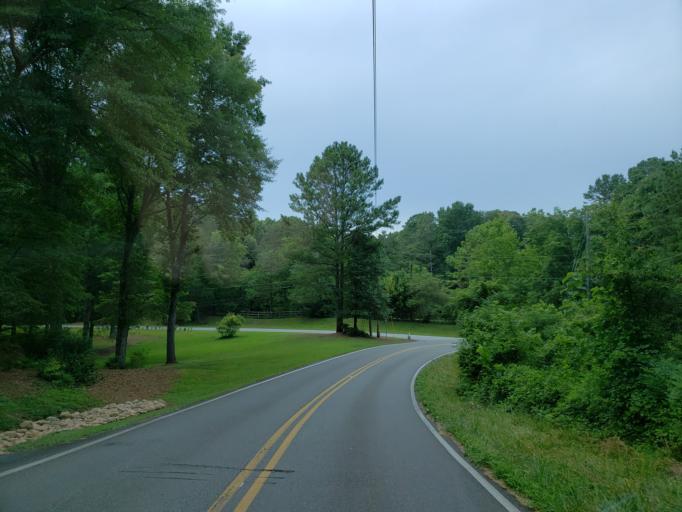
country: US
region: Georgia
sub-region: Cherokee County
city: Holly Springs
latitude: 34.1313
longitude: -84.4527
